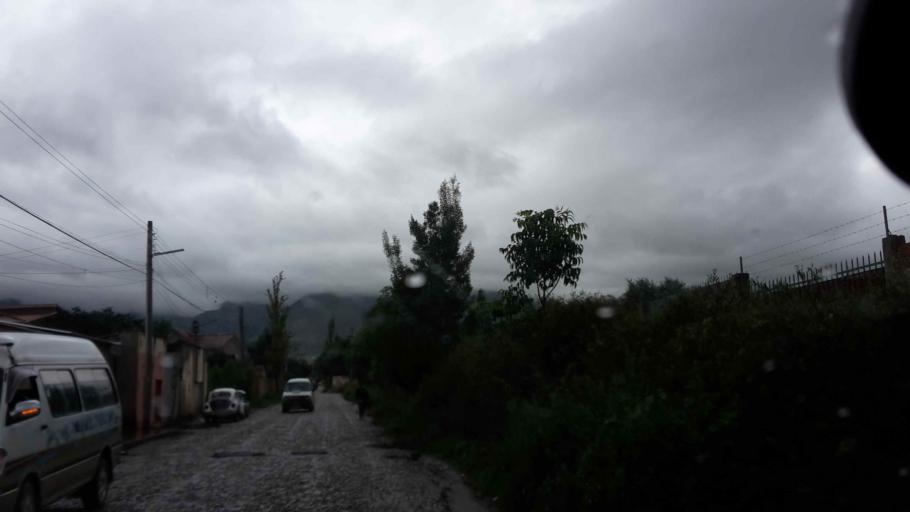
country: BO
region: Cochabamba
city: Cochabamba
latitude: -17.3630
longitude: -66.2129
